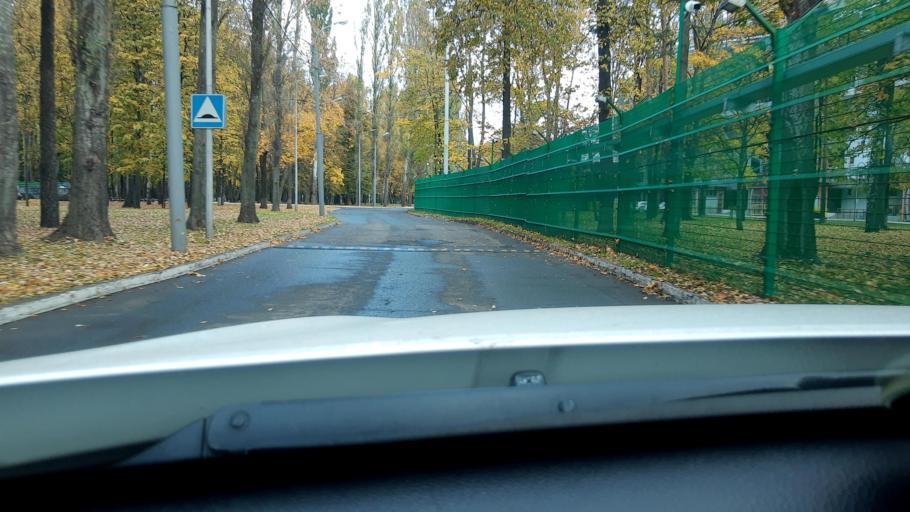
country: RU
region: Moskovskaya
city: Bogorodskoye
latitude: 55.8021
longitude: 37.7398
